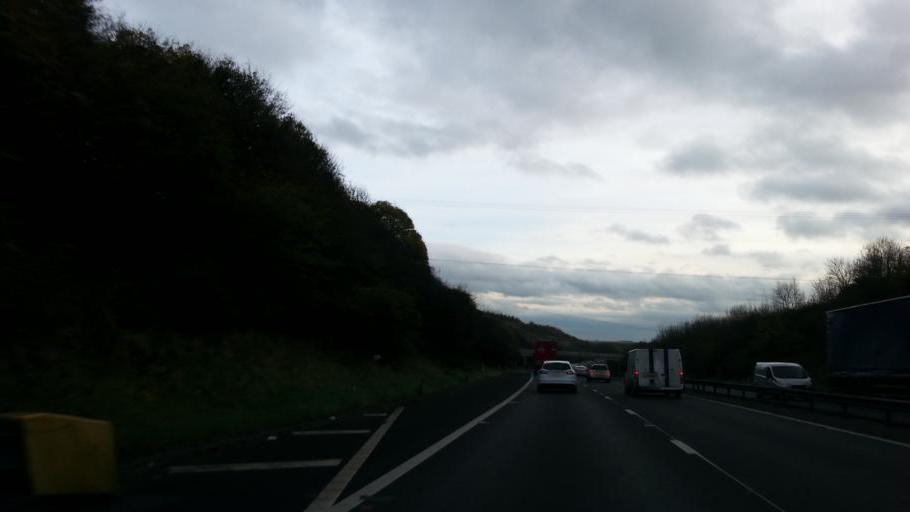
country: GB
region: England
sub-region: Doncaster
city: Marr
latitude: 53.5654
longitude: -1.2183
